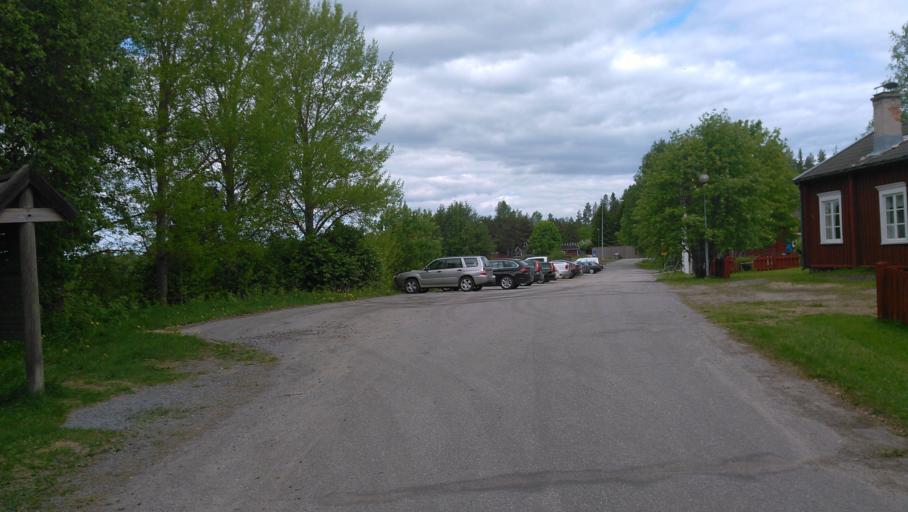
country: SE
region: Vaesterbotten
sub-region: Umea Kommun
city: Roback
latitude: 63.8593
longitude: 20.0888
